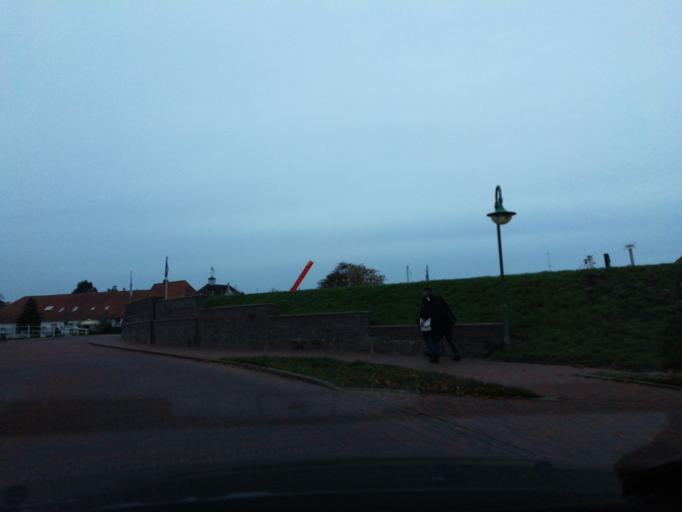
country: DE
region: Lower Saxony
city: Fedderwarden
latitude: 53.6265
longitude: 8.0289
